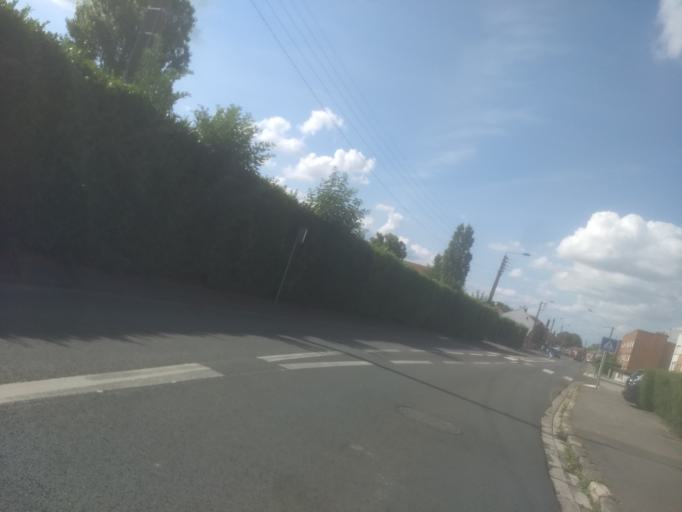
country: FR
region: Nord-Pas-de-Calais
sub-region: Departement du Pas-de-Calais
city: Beaurains
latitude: 50.2688
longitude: 2.7875
